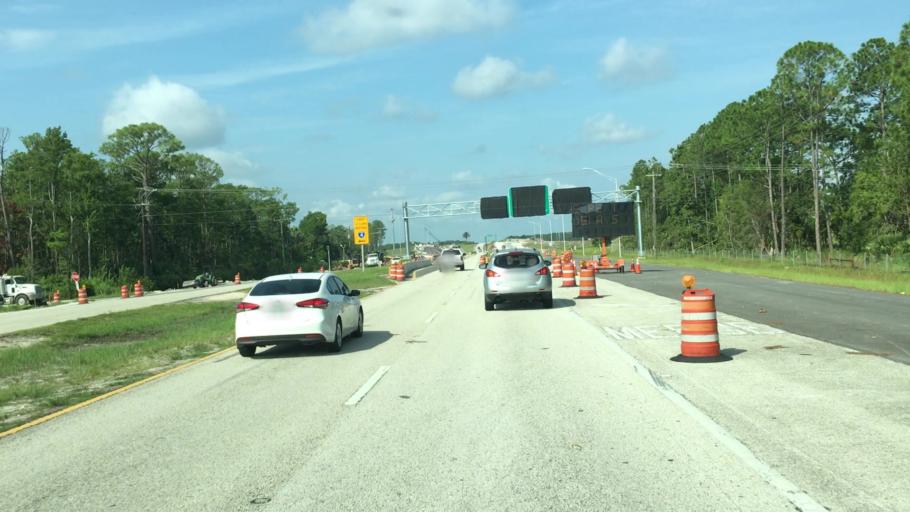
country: US
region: Florida
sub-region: Volusia County
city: South Daytona
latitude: 29.1576
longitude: -81.0690
